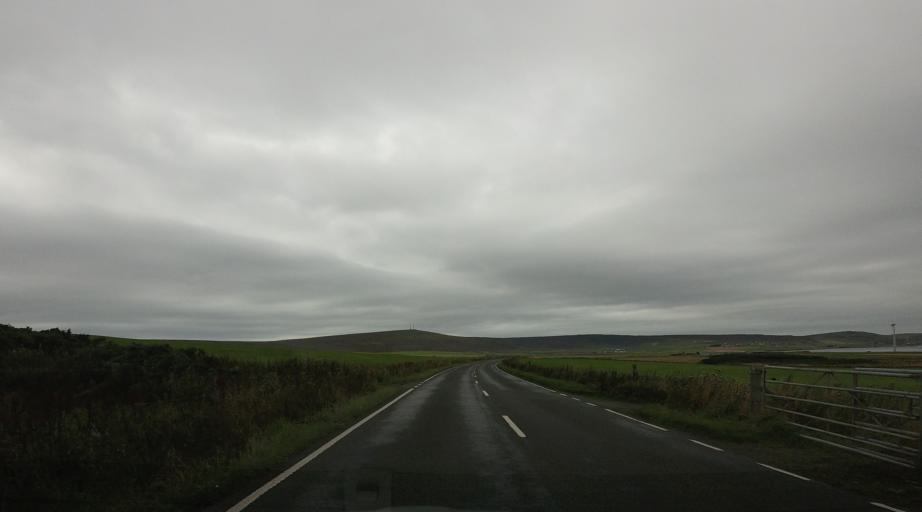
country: GB
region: Scotland
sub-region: Orkney Islands
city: Orkney
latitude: 58.9979
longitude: -3.0328
